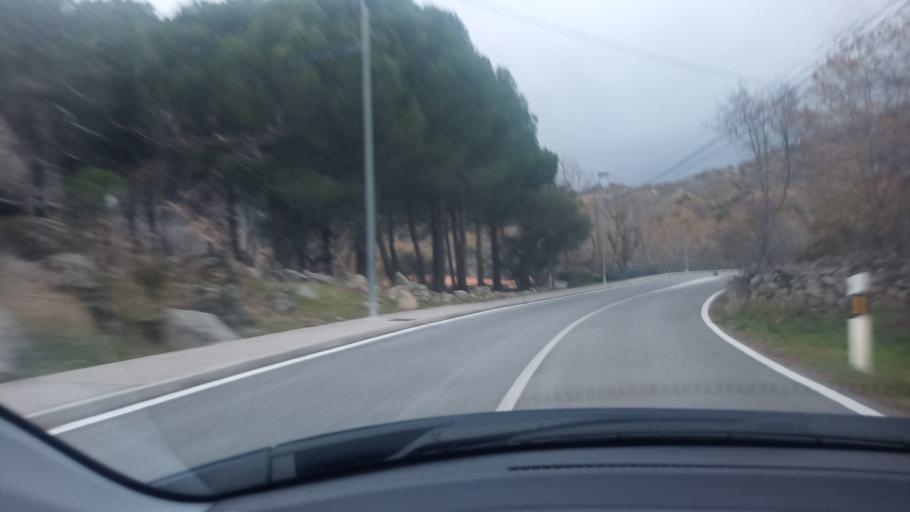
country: ES
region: Madrid
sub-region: Provincia de Madrid
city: Zarzalejo
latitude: 40.5435
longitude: -4.1724
